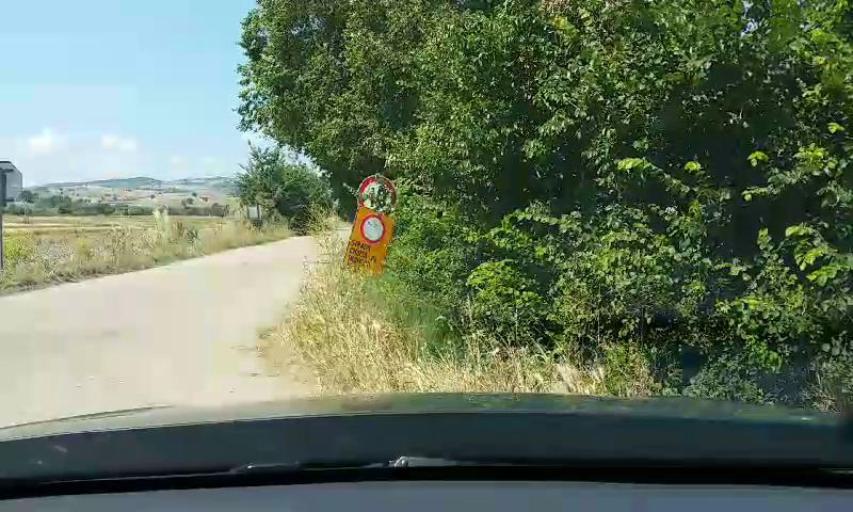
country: IT
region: Molise
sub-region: Provincia di Campobasso
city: Guglionesi
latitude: 41.9355
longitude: 14.8831
